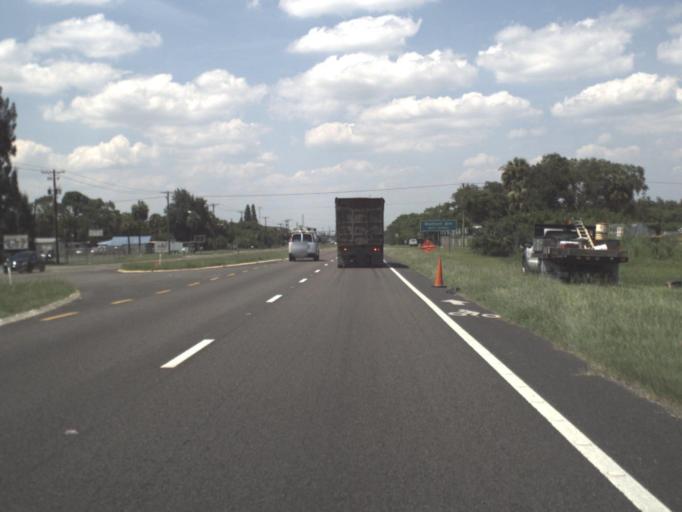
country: US
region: Florida
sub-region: Hillsborough County
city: Palm River-Clair Mel
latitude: 27.8965
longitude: -82.4017
